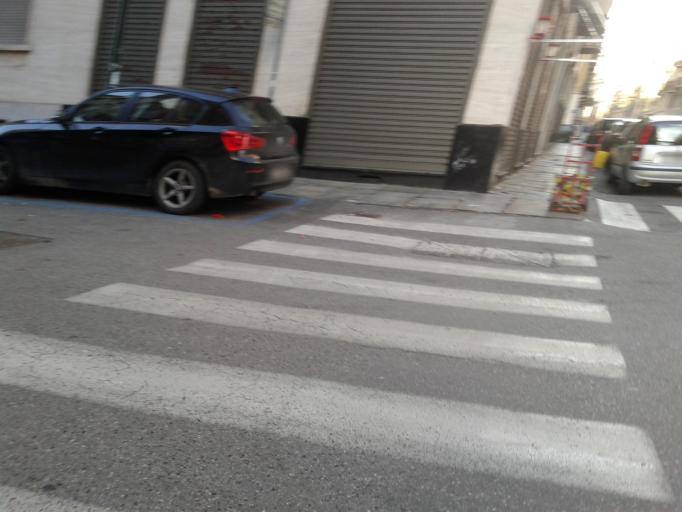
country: IT
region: Piedmont
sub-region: Provincia di Torino
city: Turin
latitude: 45.0564
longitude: 7.6615
